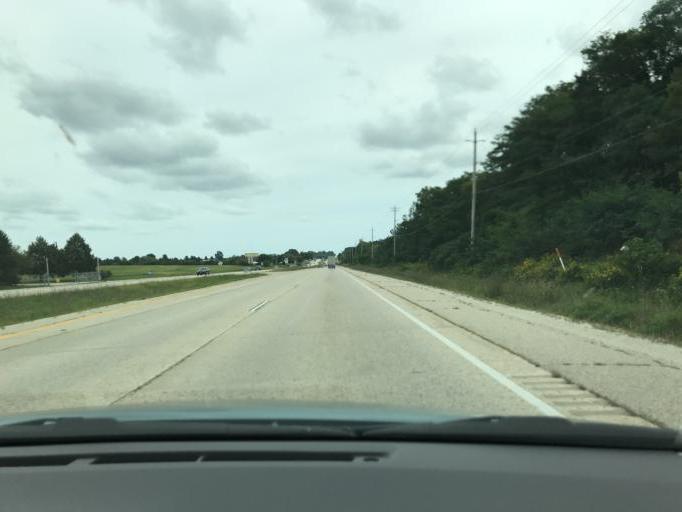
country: US
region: Wisconsin
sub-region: Kenosha County
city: Bristol
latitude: 42.5682
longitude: -88.0419
